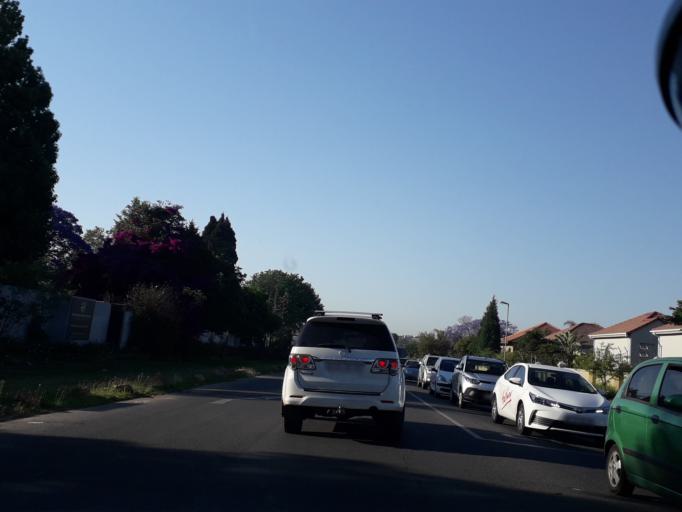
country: ZA
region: Gauteng
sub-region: City of Johannesburg Metropolitan Municipality
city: Roodepoort
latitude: -26.0864
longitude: 27.9272
